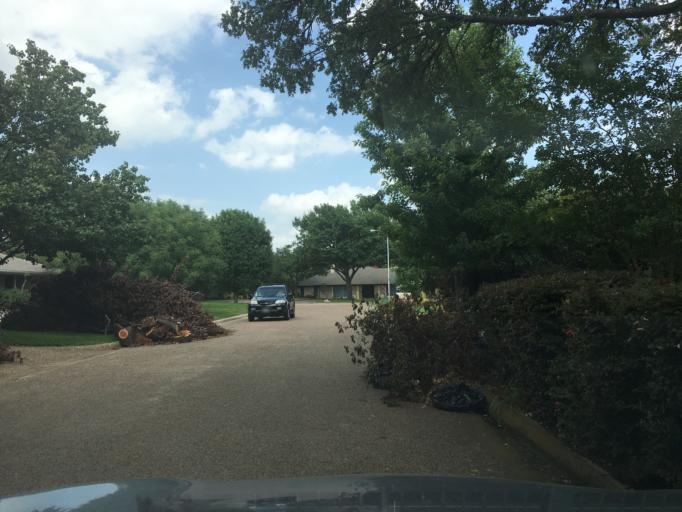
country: US
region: Texas
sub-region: Dallas County
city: University Park
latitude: 32.8975
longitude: -96.8122
